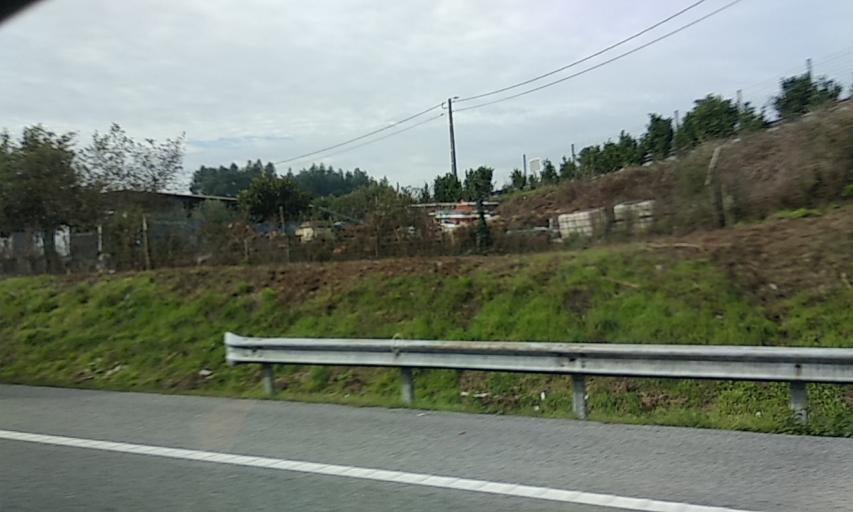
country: PT
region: Braga
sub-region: Vila Nova de Famalicao
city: Vila Nova de Famalicao
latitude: 41.3893
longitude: -8.4950
